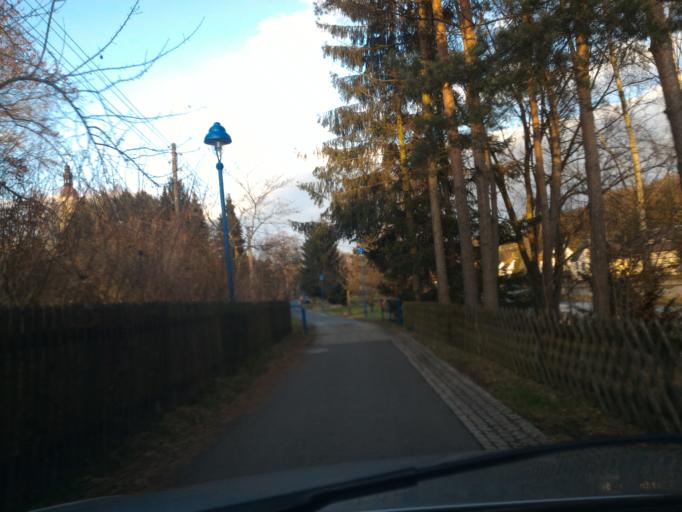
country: DE
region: Saxony
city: Hainewalde
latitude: 50.9094
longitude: 14.7017
